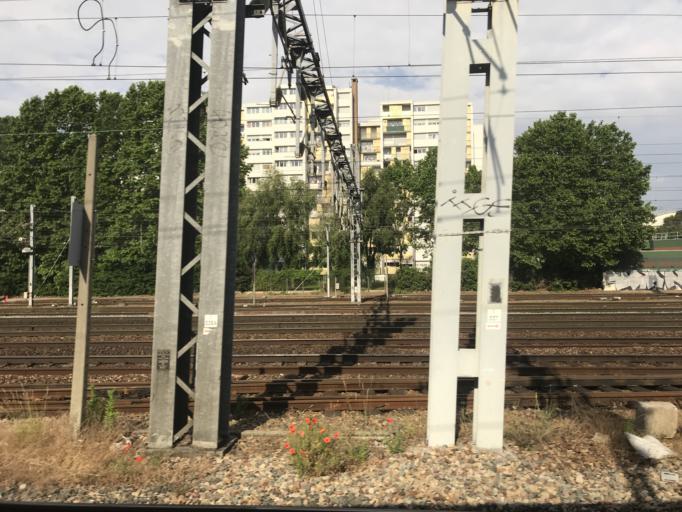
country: FR
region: Ile-de-France
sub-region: Paris
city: Saint-Ouen
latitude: 48.8964
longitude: 2.3547
